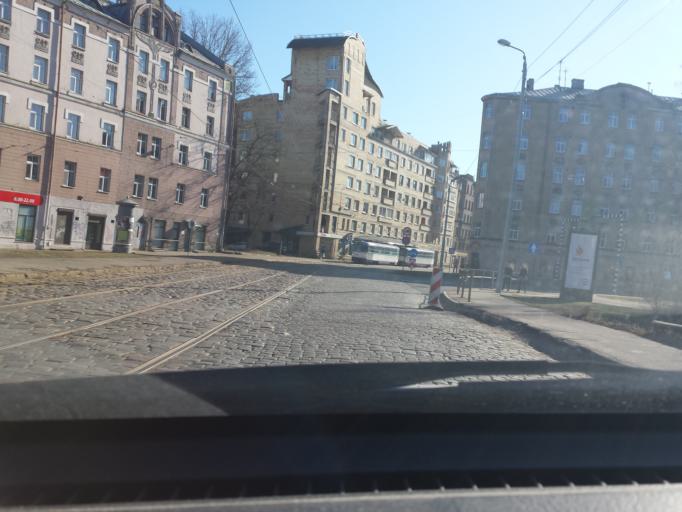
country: LV
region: Riga
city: Riga
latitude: 56.9768
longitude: 24.1454
